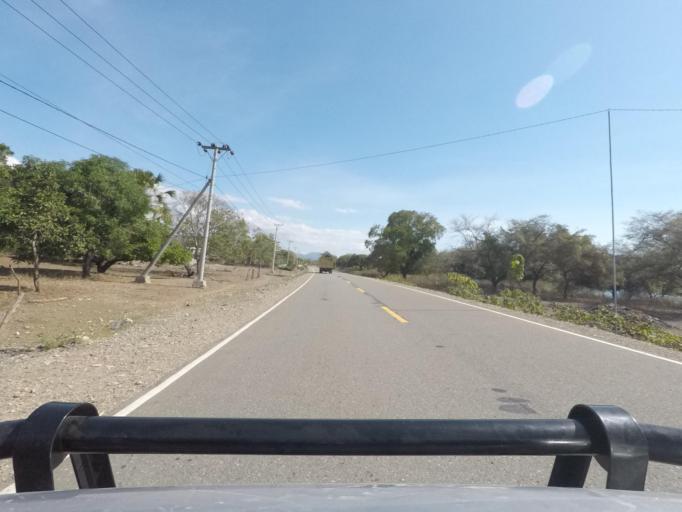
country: ID
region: East Nusa Tenggara
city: Atambua
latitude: -8.9254
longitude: 124.9878
